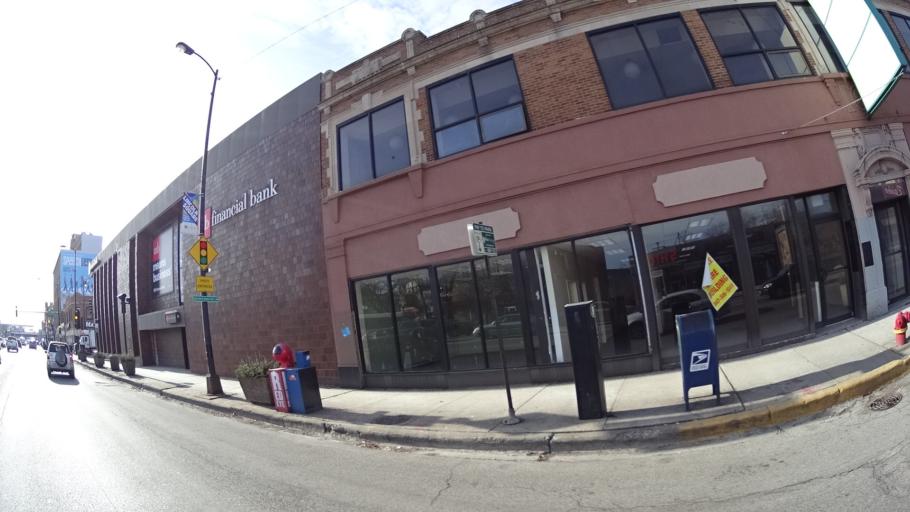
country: US
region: Illinois
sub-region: Cook County
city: Lincolnwood
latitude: 41.9692
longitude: -87.6890
